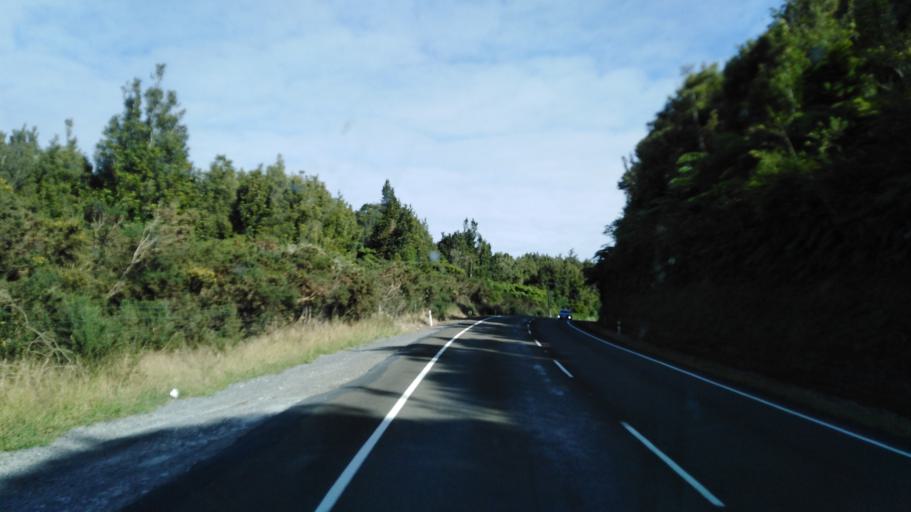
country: NZ
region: Bay of Plenty
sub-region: Tauranga City
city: Tauranga
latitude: -37.8696
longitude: 176.1338
